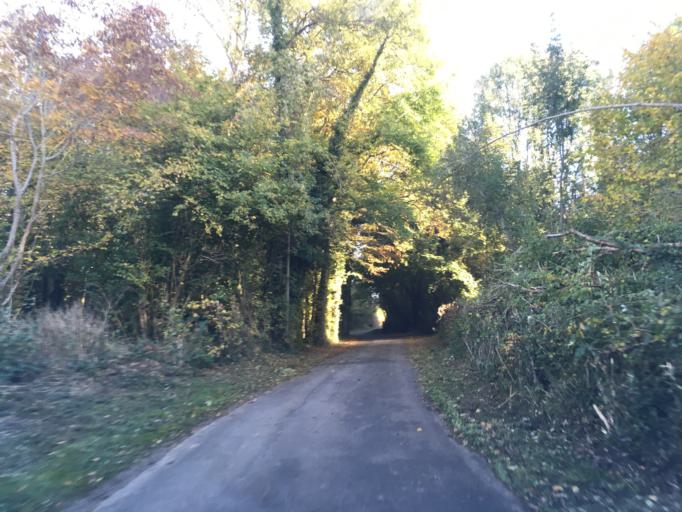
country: FR
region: Haute-Normandie
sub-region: Departement de l'Eure
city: Heudreville-sur-Eure
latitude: 49.1107
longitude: 1.2282
